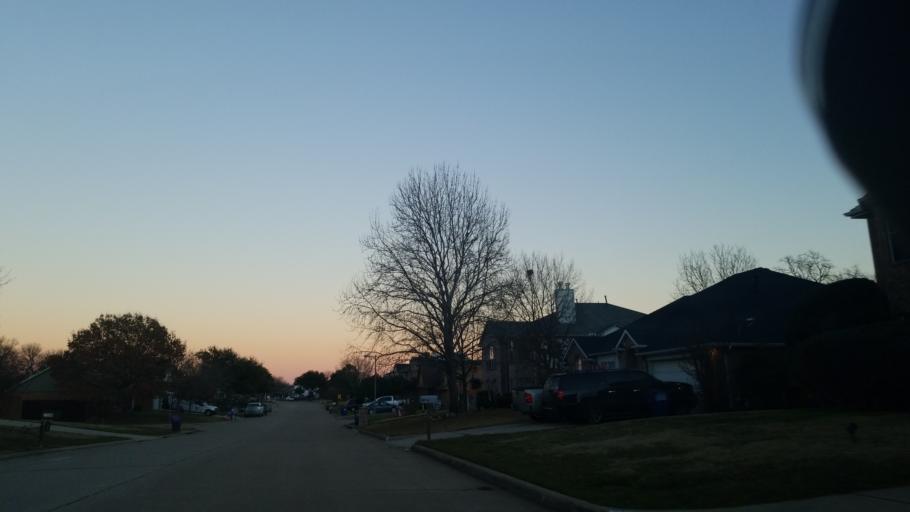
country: US
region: Texas
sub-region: Denton County
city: Hickory Creek
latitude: 33.1364
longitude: -97.0533
